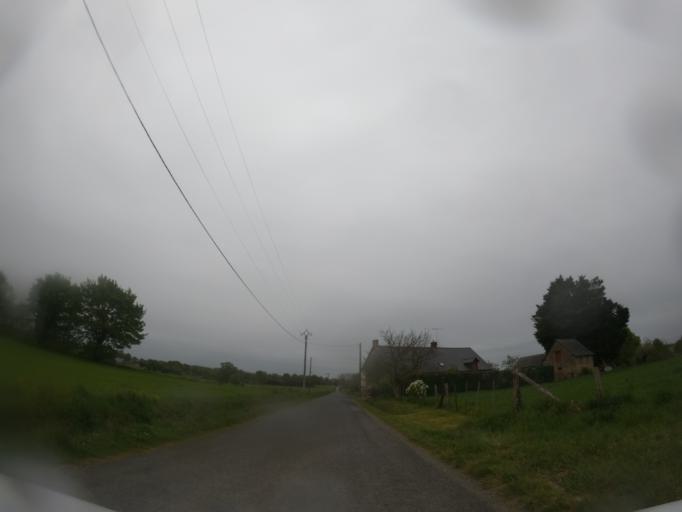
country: FR
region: Brittany
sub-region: Departement d'Ille-et-Vilaine
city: La Guerche-de-Bretagne
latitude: 47.9558
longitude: -1.1291
